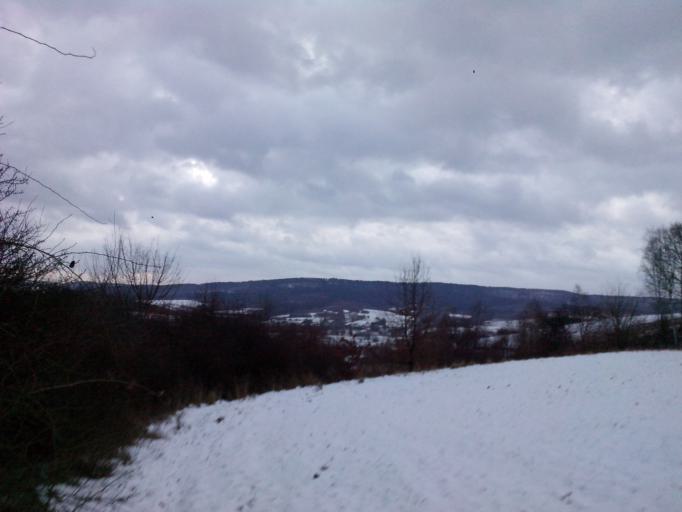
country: PL
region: Subcarpathian Voivodeship
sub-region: Powiat strzyzowski
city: Jawornik
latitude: 49.8411
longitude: 21.8426
